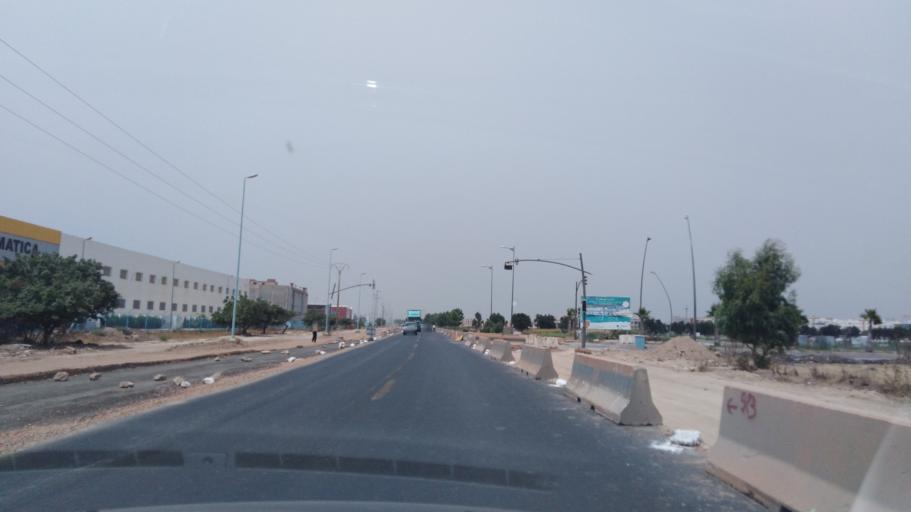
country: MA
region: Grand Casablanca
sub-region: Mediouna
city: Mediouna
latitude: 33.3897
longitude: -7.5360
